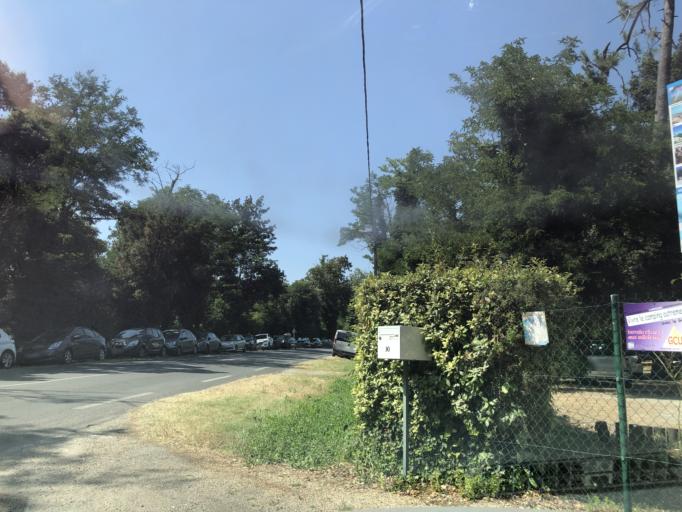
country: FR
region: Poitou-Charentes
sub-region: Departement de la Charente-Maritime
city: Meschers-sur-Gironde
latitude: 45.5670
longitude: -0.9710
